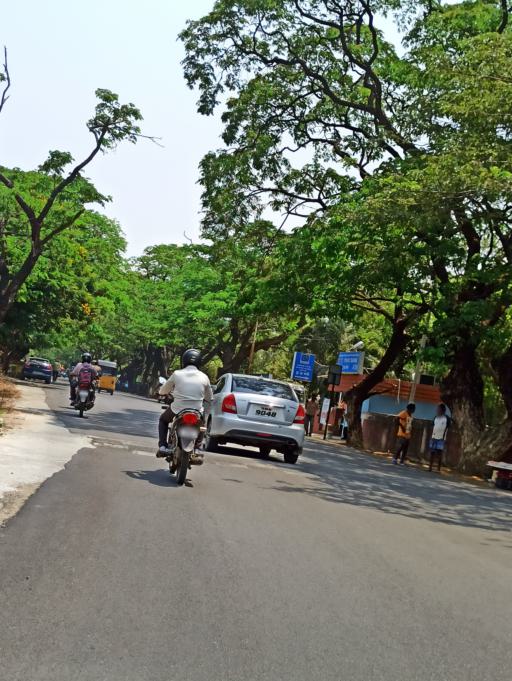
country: IN
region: Tamil Nadu
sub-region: Thiruvallur
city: Chinnasekkadu
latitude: 13.1524
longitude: 80.2428
